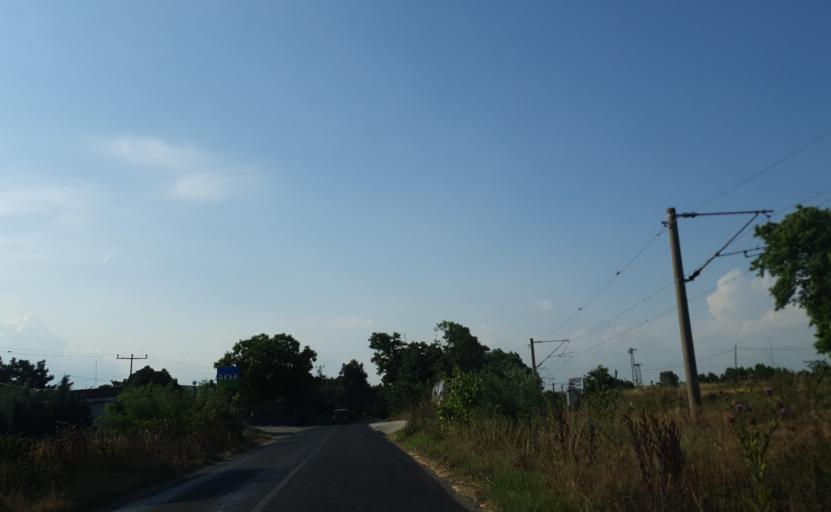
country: TR
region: Tekirdag
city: Muratli
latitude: 41.1916
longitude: 27.4765
